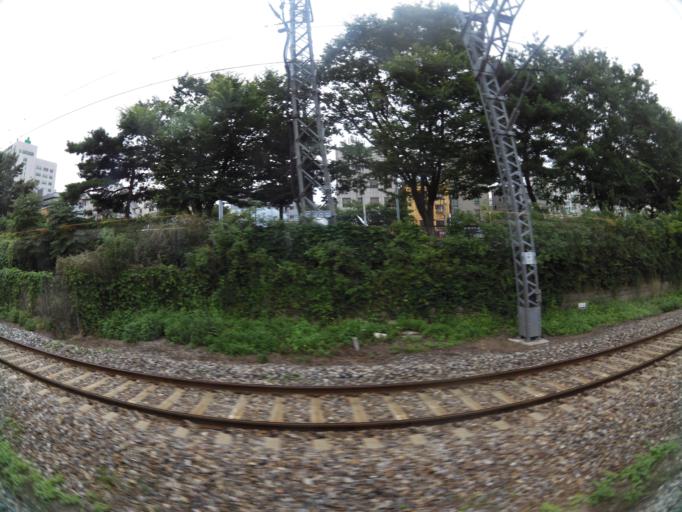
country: KR
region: Gyeonggi-do
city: Anyang-si
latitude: 37.3602
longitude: 126.9486
